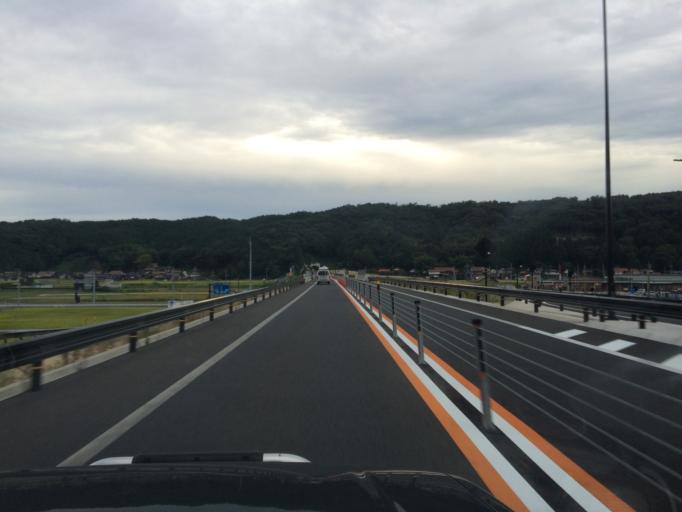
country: JP
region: Tottori
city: Tottori
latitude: 35.4985
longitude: 134.0501
